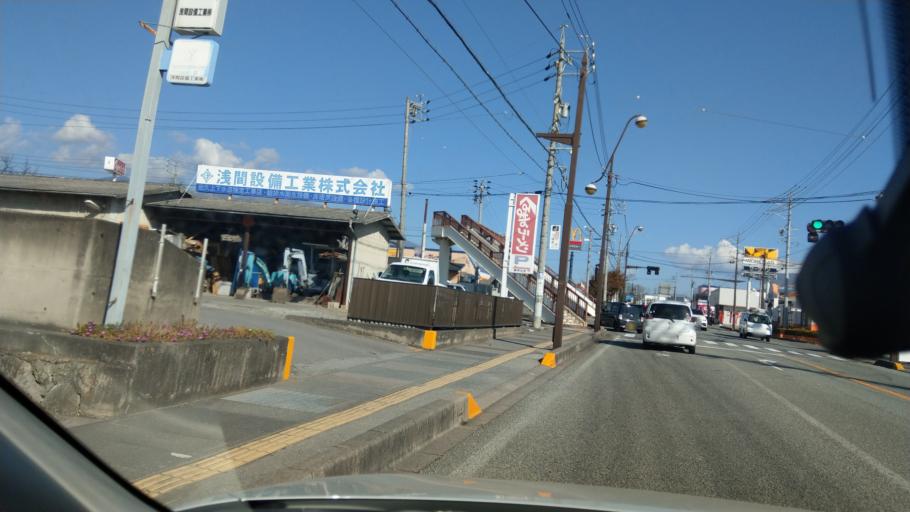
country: JP
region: Nagano
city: Komoro
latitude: 36.2829
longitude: 138.4823
